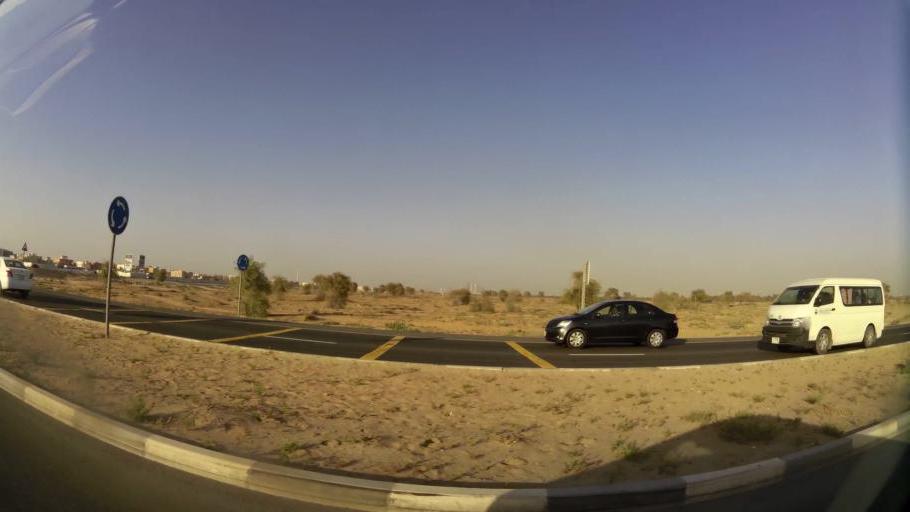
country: AE
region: Ajman
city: Ajman
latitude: 25.3734
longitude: 55.5091
